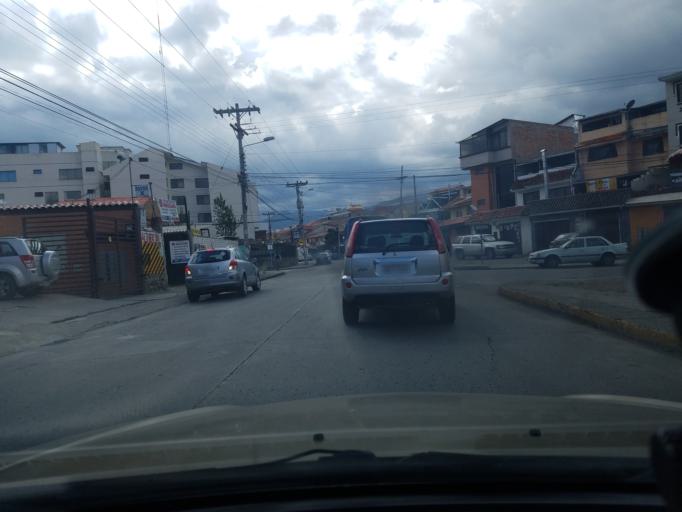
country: EC
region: Azuay
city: Cuenca
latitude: -2.9037
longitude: -78.9938
